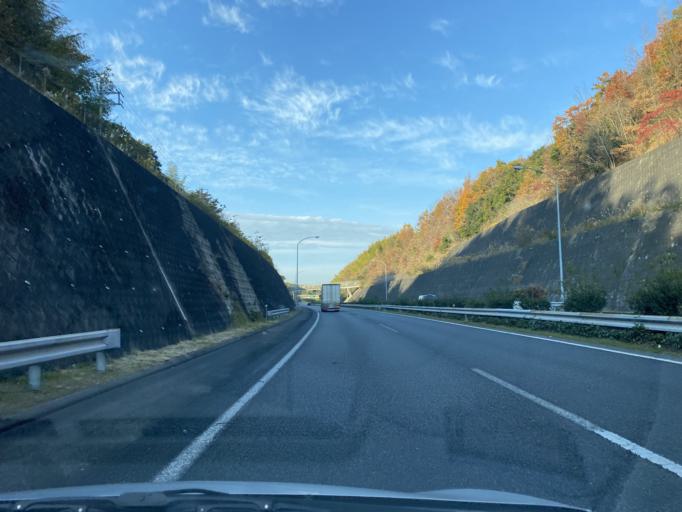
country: JP
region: Osaka
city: Izumi
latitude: 34.4145
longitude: 135.4489
